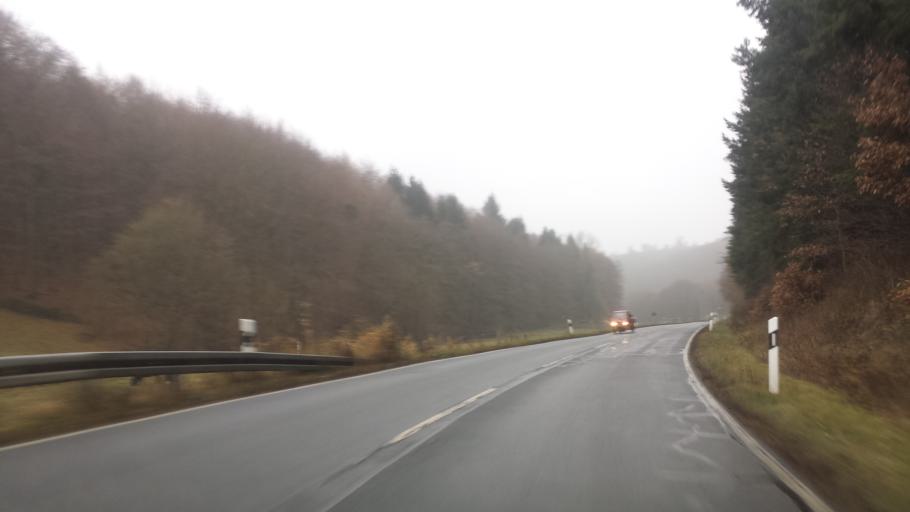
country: DE
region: Hesse
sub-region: Regierungsbezirk Darmstadt
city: Seeheim-Jugenheim
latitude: 49.7690
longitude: 8.6758
